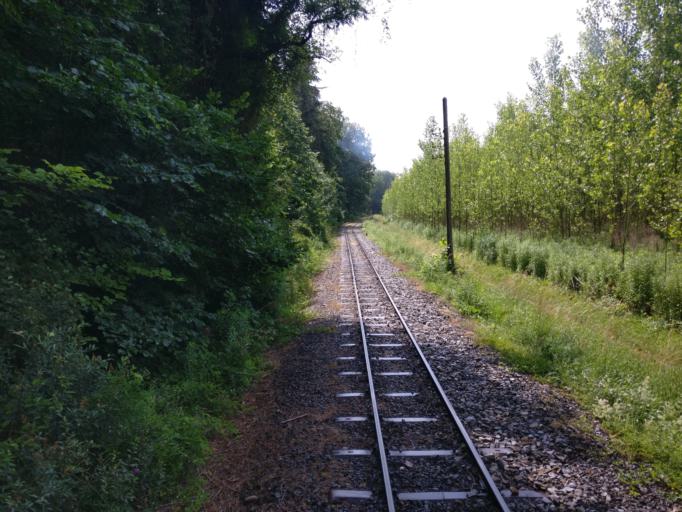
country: AT
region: Upper Austria
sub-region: Politischer Bezirk Steyr-Land
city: Garsten
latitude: 48.0477
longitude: 14.3659
